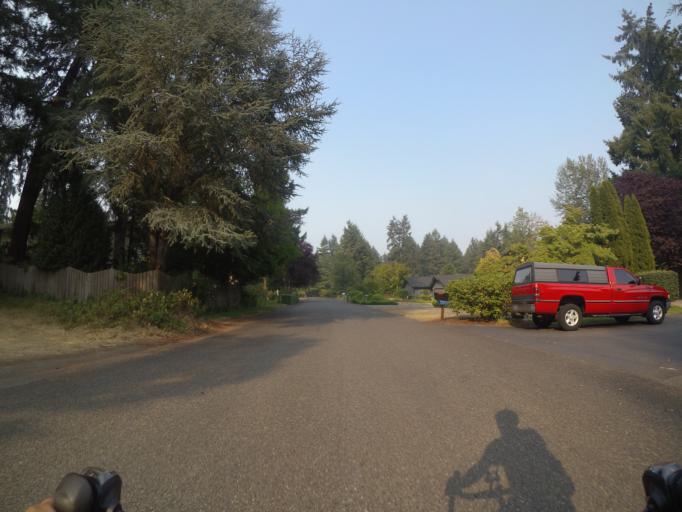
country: US
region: Washington
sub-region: Pierce County
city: Lakewood
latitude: 47.1438
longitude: -122.5201
